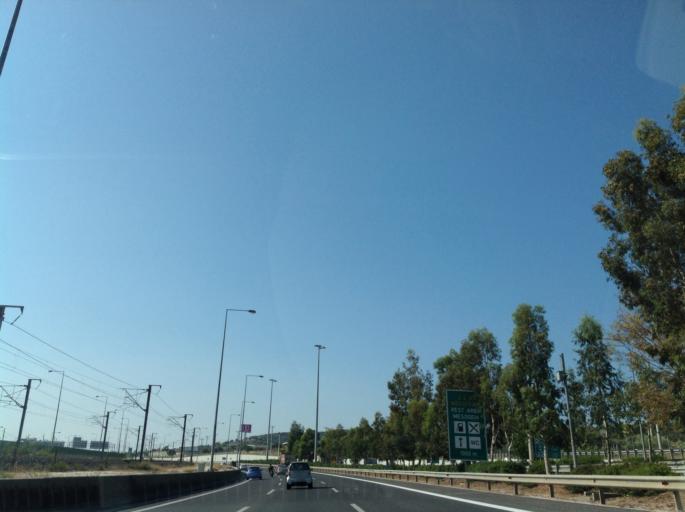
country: GR
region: Attica
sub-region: Nomarchia Anatolikis Attikis
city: Leondarion
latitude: 37.9820
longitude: 23.8697
